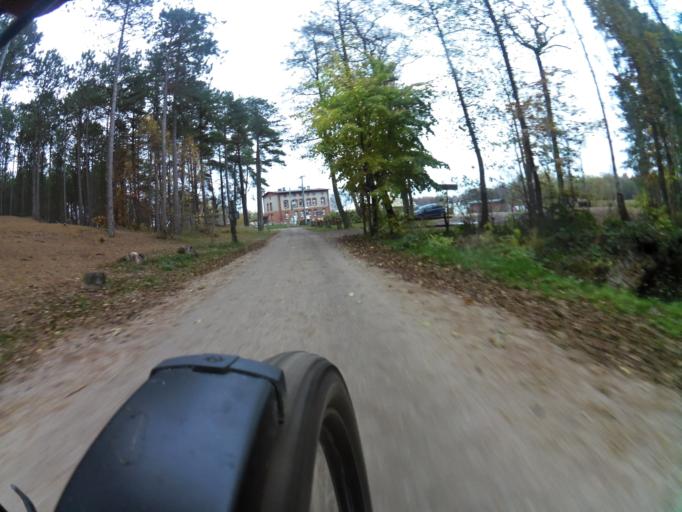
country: PL
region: Pomeranian Voivodeship
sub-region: Powiat wejherowski
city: Choczewo
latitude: 54.7812
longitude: 17.7370
